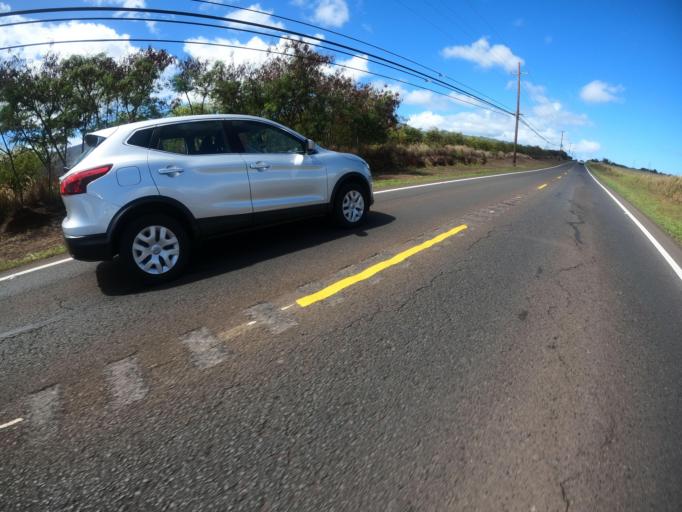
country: US
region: Hawaii
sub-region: Honolulu County
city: Village Park
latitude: 21.4064
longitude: -158.0424
